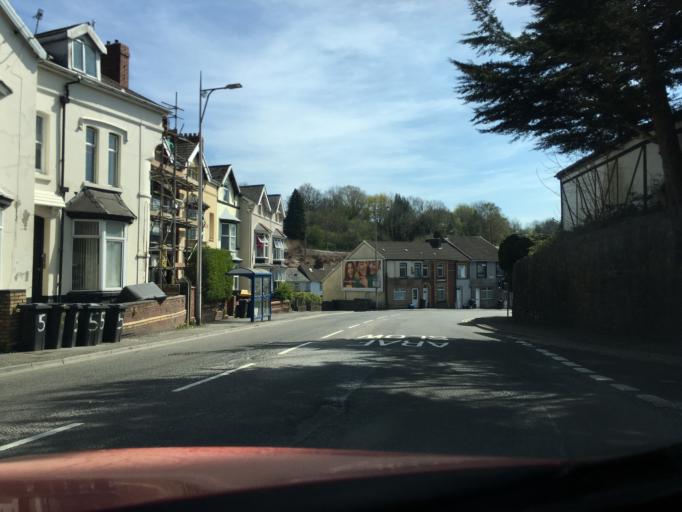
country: GB
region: Wales
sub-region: Merthyr Tydfil County Borough
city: Merthyr Tydfil
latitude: 51.7528
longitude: -3.3744
